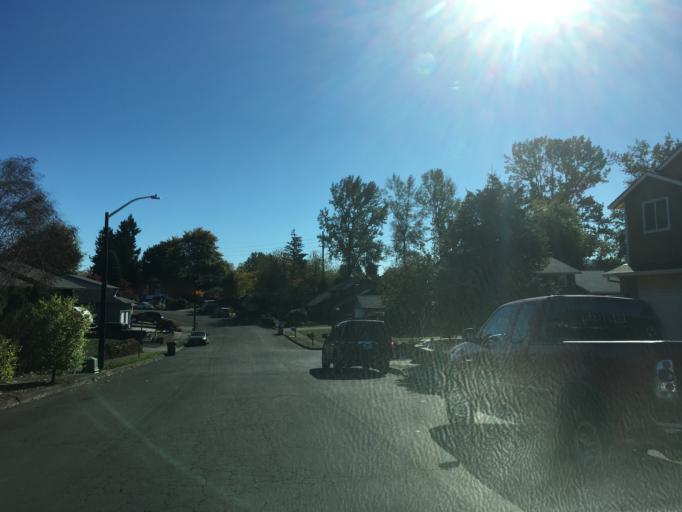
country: US
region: Oregon
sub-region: Multnomah County
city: Gresham
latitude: 45.4914
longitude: -122.4008
